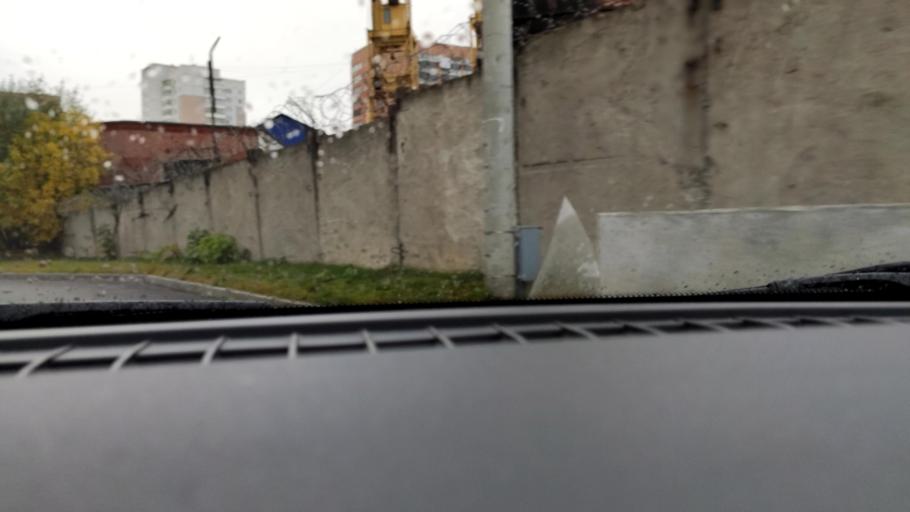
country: RU
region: Perm
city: Perm
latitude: 57.9970
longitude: 56.2016
